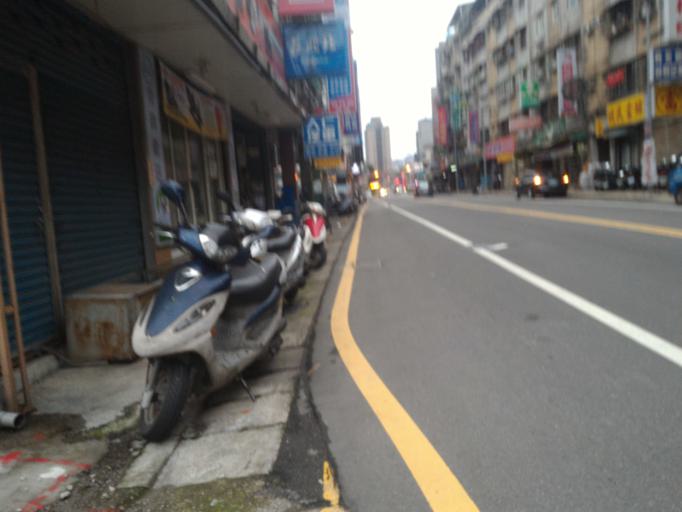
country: TW
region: Taipei
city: Taipei
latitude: 24.9859
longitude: 121.5410
